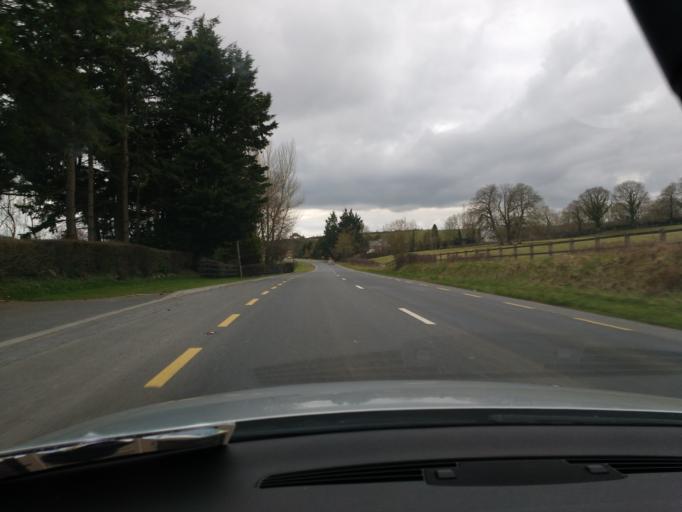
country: IE
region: Leinster
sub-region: Kilkenny
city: Kilkenny
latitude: 52.6810
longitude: -7.2745
